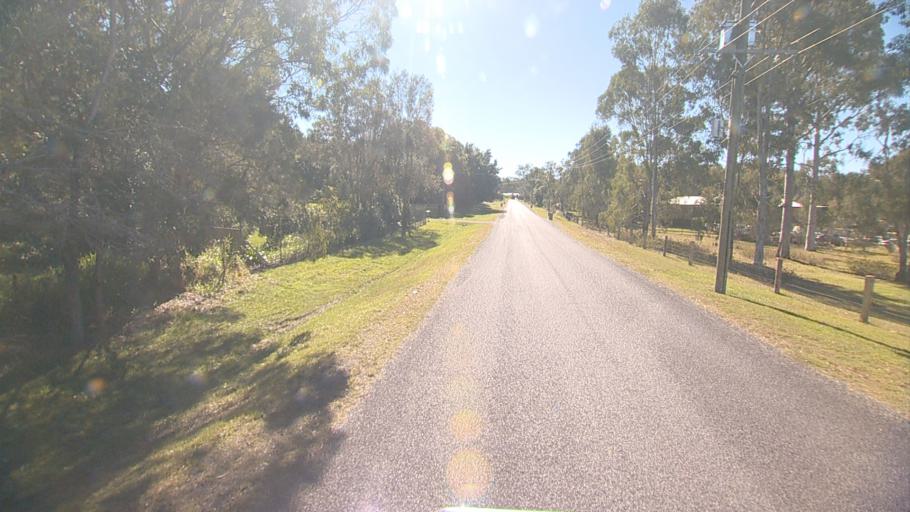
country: AU
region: Queensland
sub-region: Logan
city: Park Ridge South
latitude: -27.7130
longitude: 153.0410
